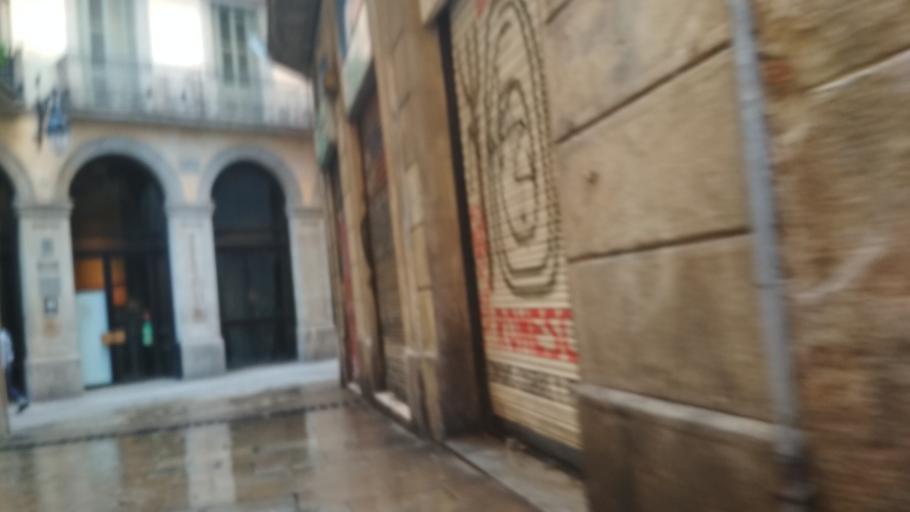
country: ES
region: Catalonia
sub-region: Provincia de Barcelona
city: Ciutat Vella
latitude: 41.3801
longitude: 2.1726
